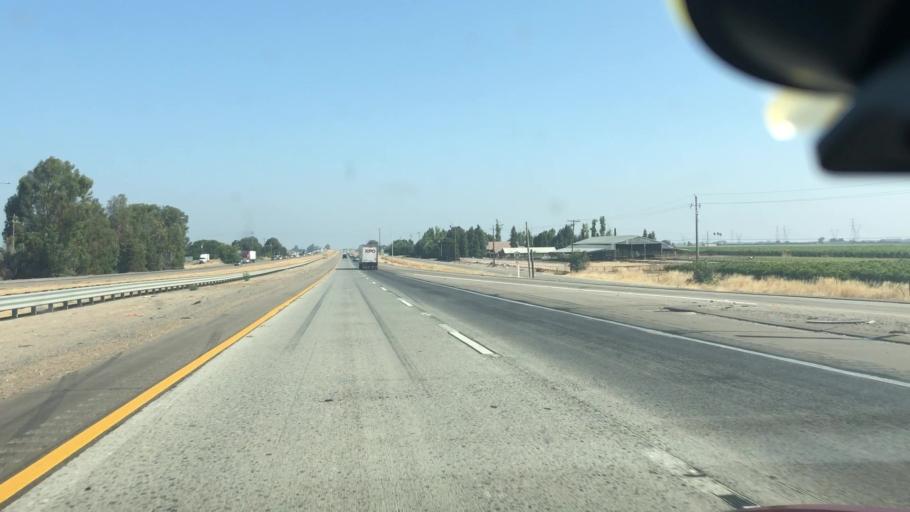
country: US
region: California
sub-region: San Joaquin County
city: Thornton
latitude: 38.1483
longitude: -121.3991
